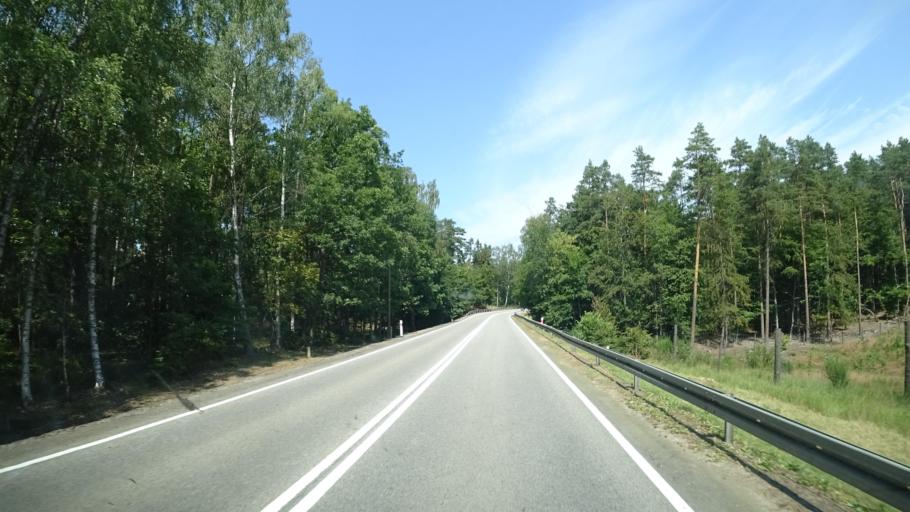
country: PL
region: Pomeranian Voivodeship
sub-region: Powiat koscierski
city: Grabowo Koscierskie
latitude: 54.2103
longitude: 18.1140
